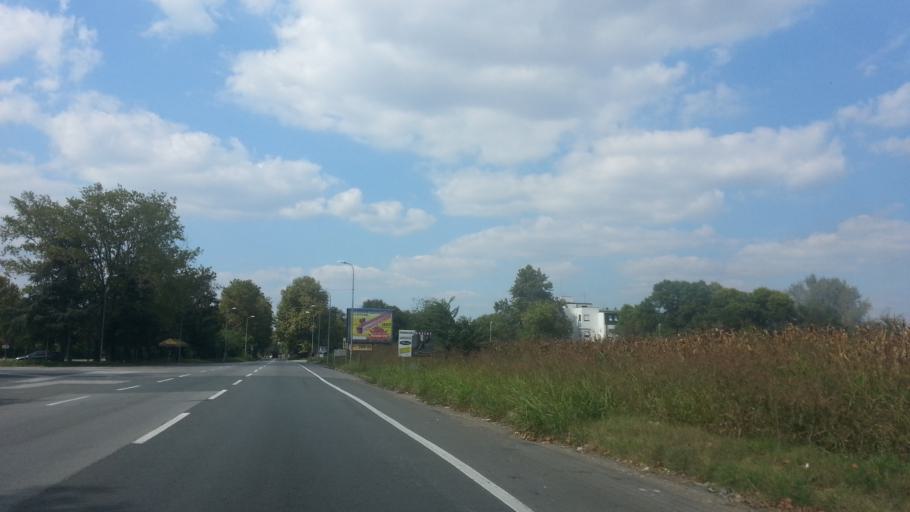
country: RS
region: Central Serbia
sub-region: Belgrade
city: Zemun
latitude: 44.8733
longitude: 20.3454
